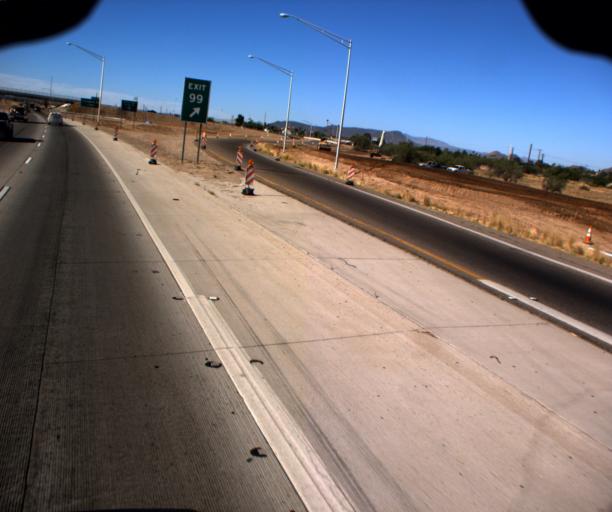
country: US
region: Arizona
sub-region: Pima County
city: South Tucson
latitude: 32.1811
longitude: -110.9857
